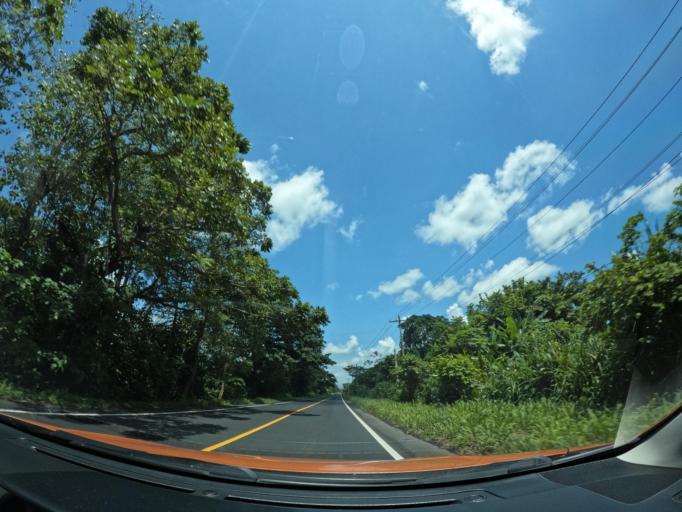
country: GT
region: Escuintla
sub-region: Municipio de Masagua
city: Masagua
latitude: 14.1689
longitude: -90.8766
